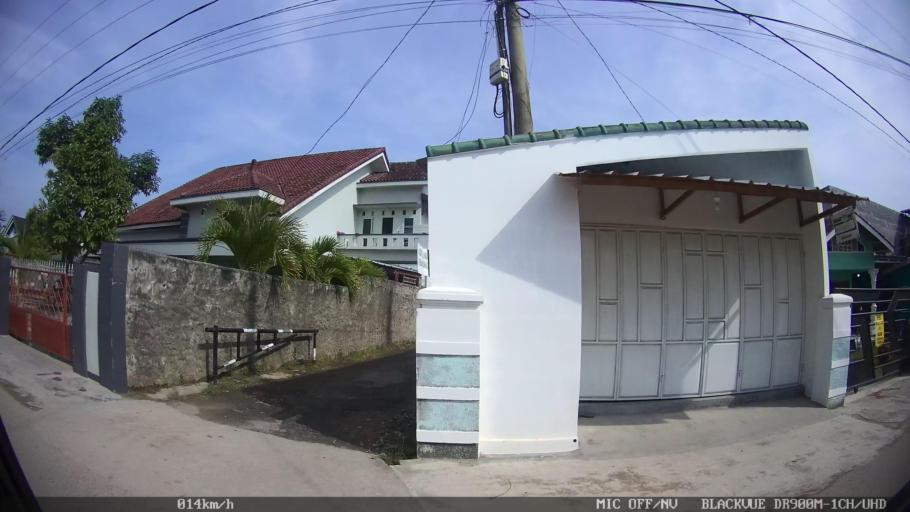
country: ID
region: Lampung
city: Kedaton
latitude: -5.3795
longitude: 105.2994
